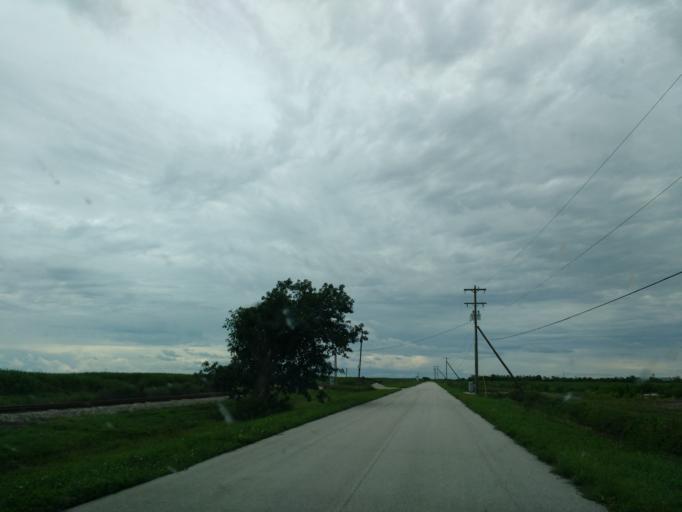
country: US
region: Florida
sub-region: Glades County
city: Moore Haven
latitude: 26.8163
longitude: -81.0744
